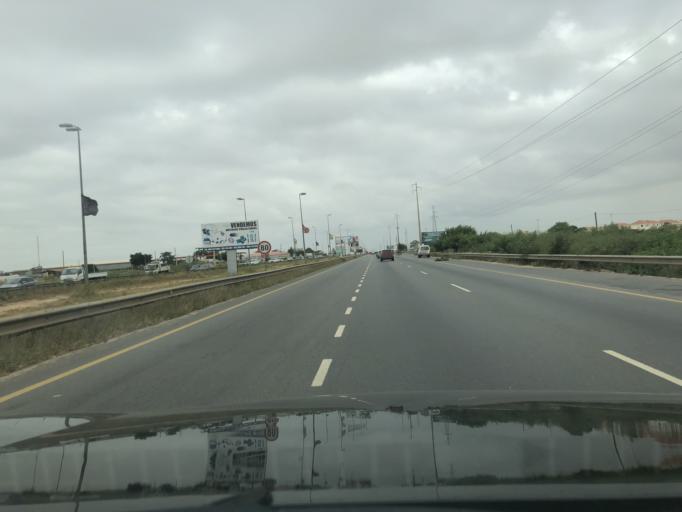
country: AO
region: Luanda
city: Luanda
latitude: -8.9733
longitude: 13.2436
